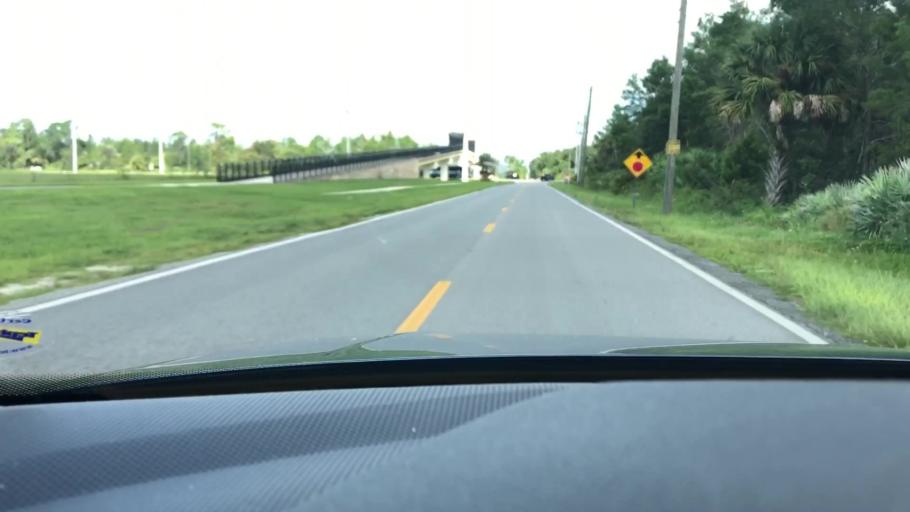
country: US
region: Florida
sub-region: Volusia County
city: Edgewater
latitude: 28.9490
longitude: -80.9446
